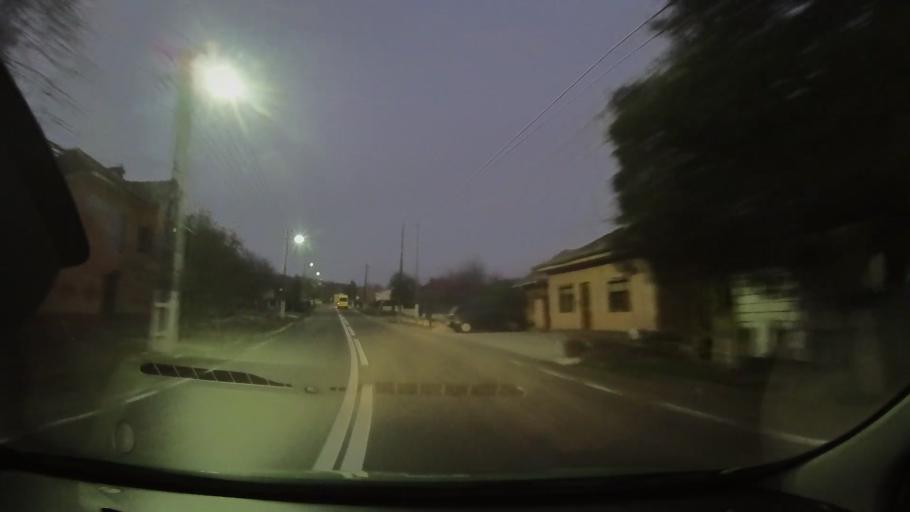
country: RO
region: Constanta
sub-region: Comuna Ion Corvin
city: Ion Corvin
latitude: 44.1107
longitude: 27.8042
